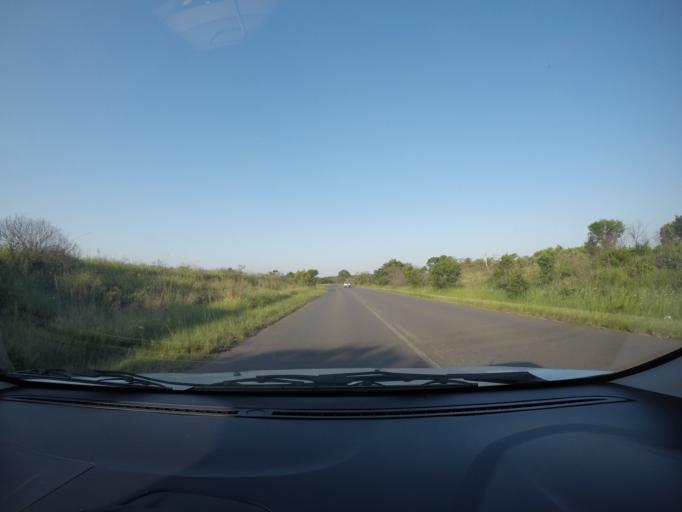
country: ZA
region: KwaZulu-Natal
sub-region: uThungulu District Municipality
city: Richards Bay
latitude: -28.7527
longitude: 32.0092
